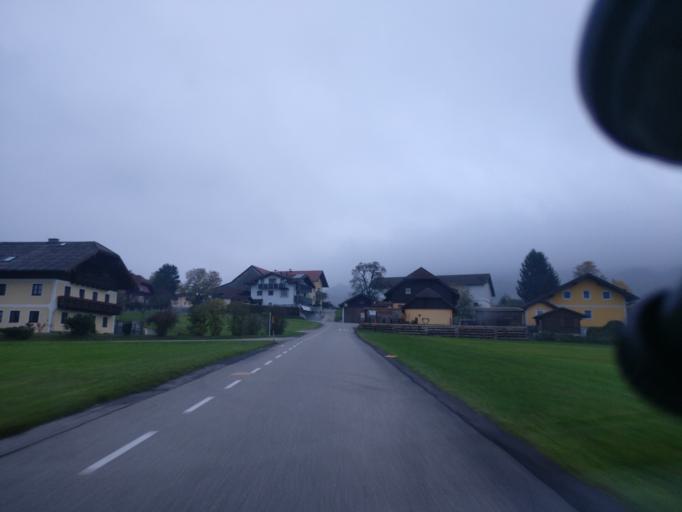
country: AT
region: Salzburg
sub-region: Politischer Bezirk Salzburg-Umgebung
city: Hallwang
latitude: 47.8485
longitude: 13.0948
